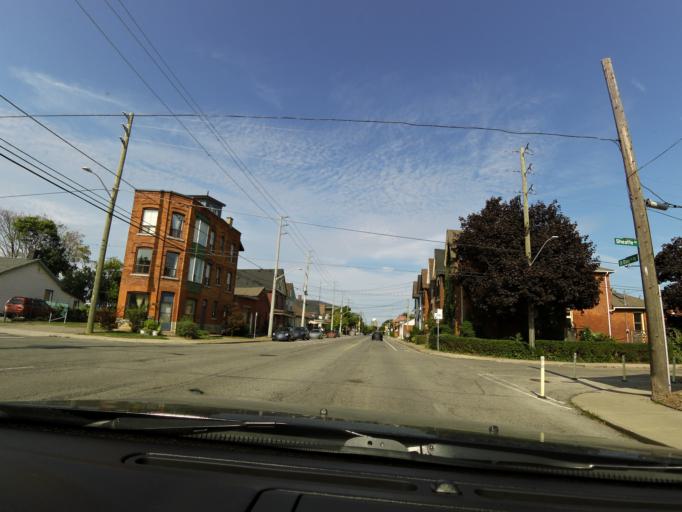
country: CA
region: Ontario
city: Hamilton
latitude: 43.2637
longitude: -79.8715
